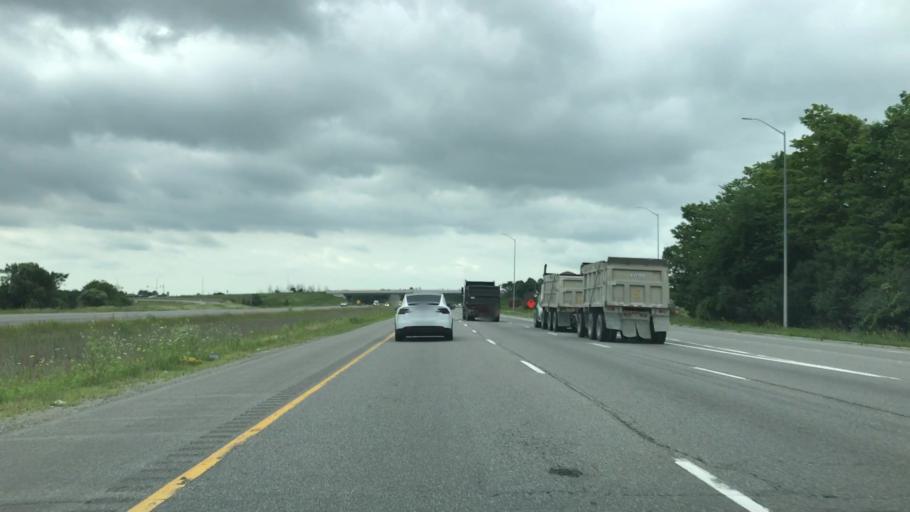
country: CA
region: Ontario
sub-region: York
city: Richmond Hill
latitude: 43.9442
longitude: -79.3909
